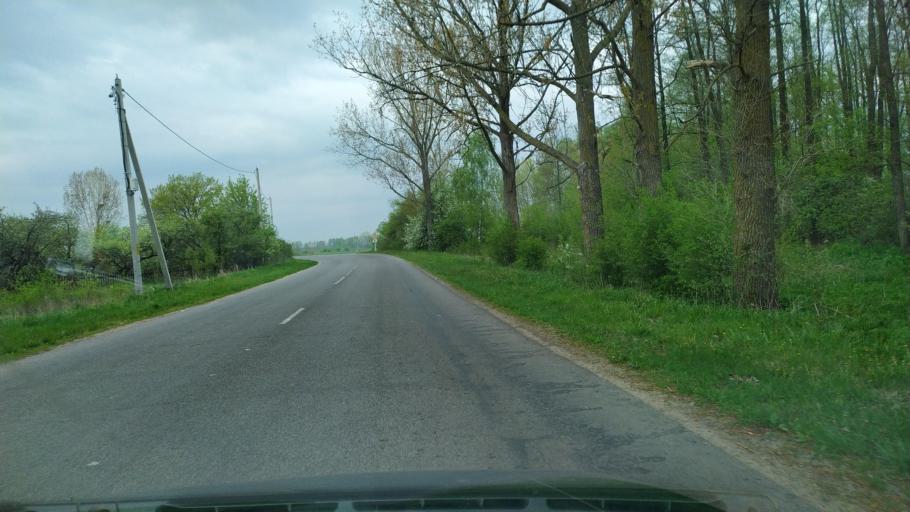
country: BY
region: Brest
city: Zhabinka
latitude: 52.1557
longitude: 24.0972
